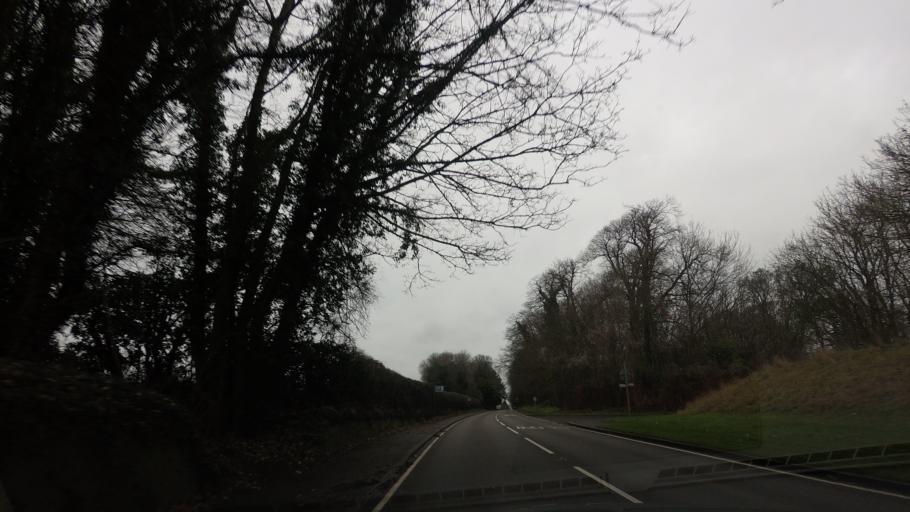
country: GB
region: England
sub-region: Kent
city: Maidstone
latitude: 51.2246
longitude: 0.5106
